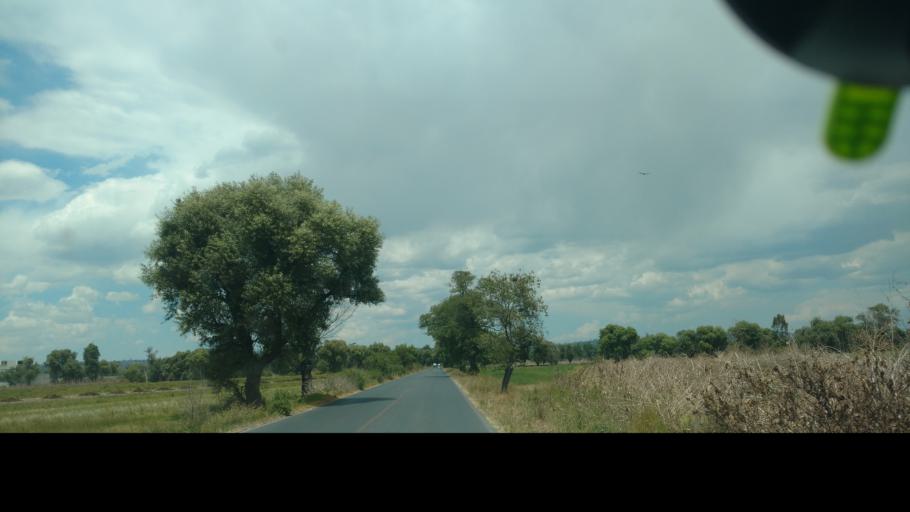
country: MX
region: Tlaxcala
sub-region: Tetlatlahuca
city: Tetlatlahuca
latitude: 19.1975
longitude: -98.2857
